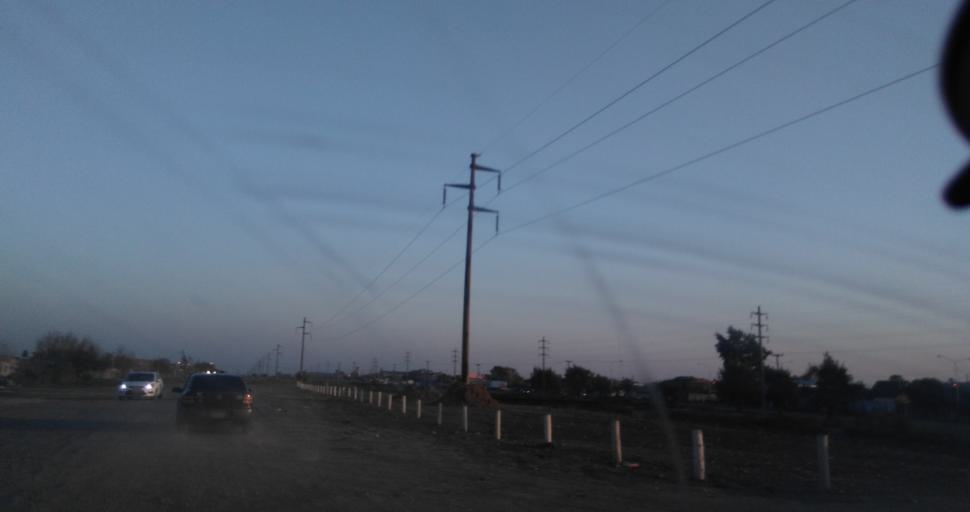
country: AR
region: Chaco
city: Resistencia
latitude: -27.4798
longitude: -58.9988
